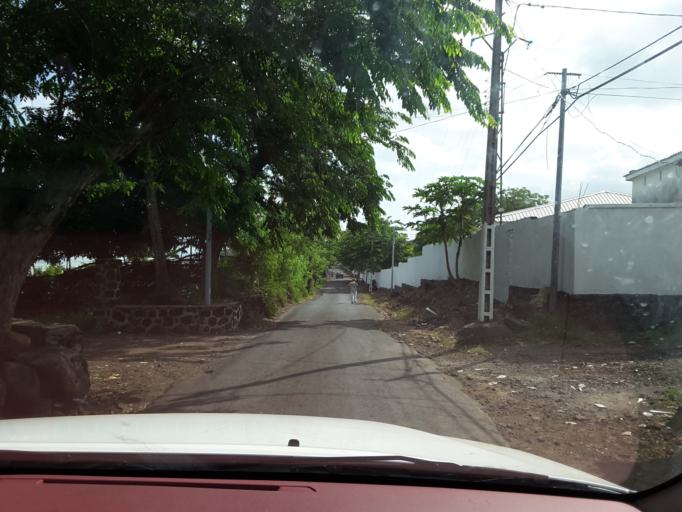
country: KM
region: Grande Comore
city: Mitsamiouli
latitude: -11.3938
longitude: 43.2853
